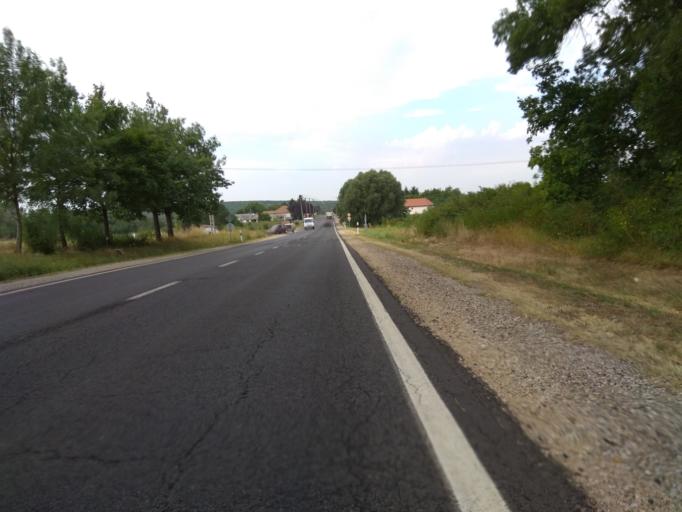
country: HU
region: Borsod-Abauj-Zemplen
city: Harsany
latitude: 47.9225
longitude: 20.7491
